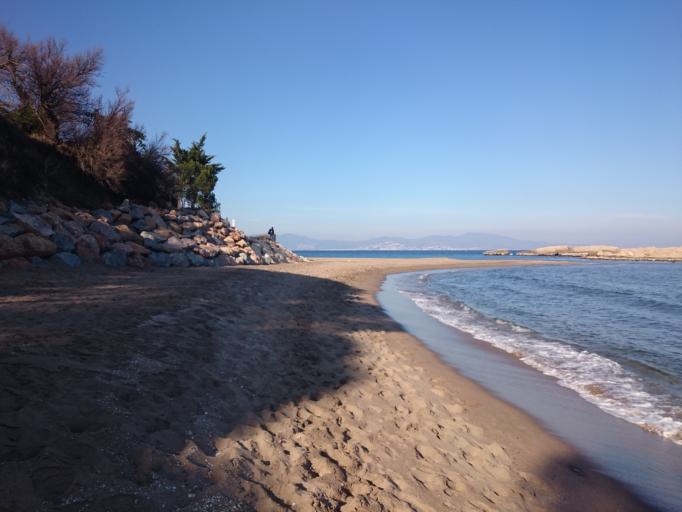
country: ES
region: Catalonia
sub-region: Provincia de Girona
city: l'Escala
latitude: 42.1348
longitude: 3.1218
